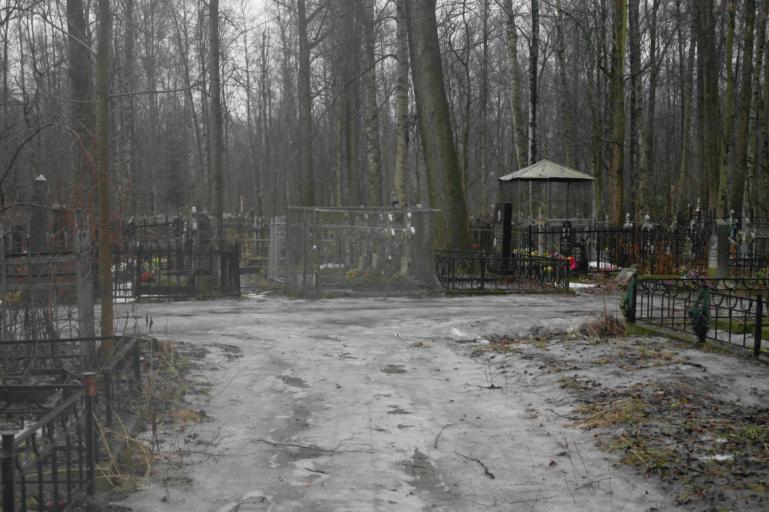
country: RU
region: St.-Petersburg
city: Komendantsky aerodrom
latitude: 59.9940
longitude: 30.2643
